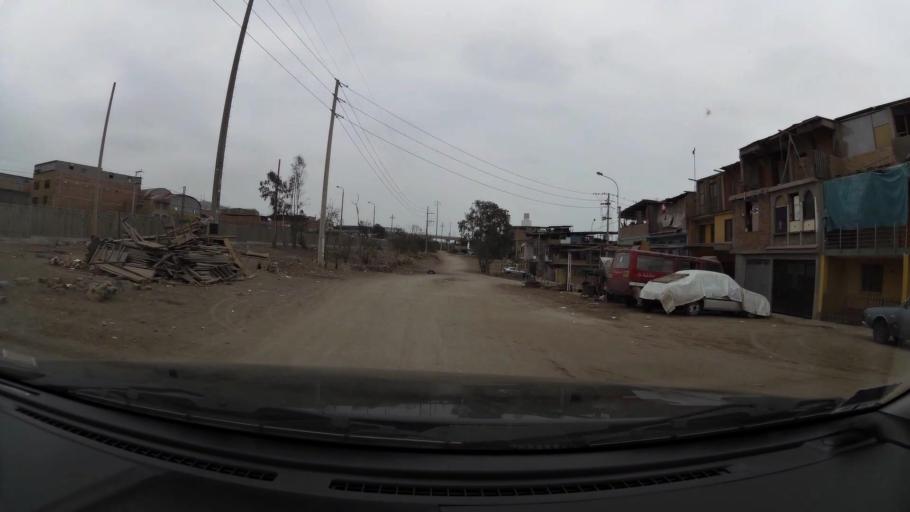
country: PE
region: Lima
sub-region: Lima
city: Surco
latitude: -12.2001
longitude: -76.9381
